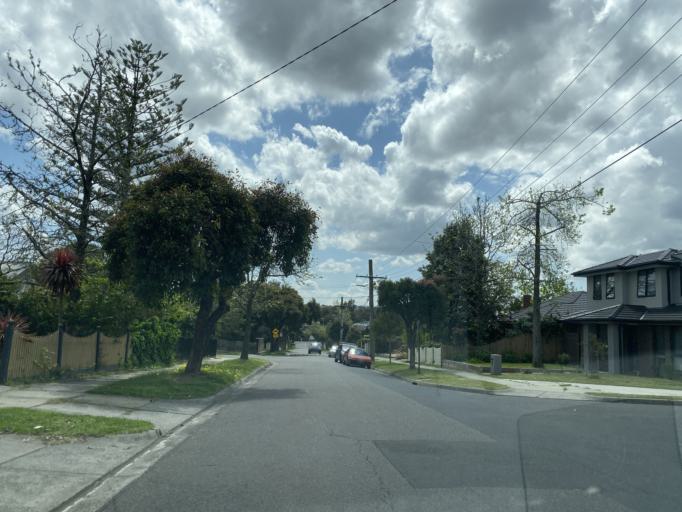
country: AU
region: Victoria
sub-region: Monash
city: Ashwood
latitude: -37.8570
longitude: 145.1078
